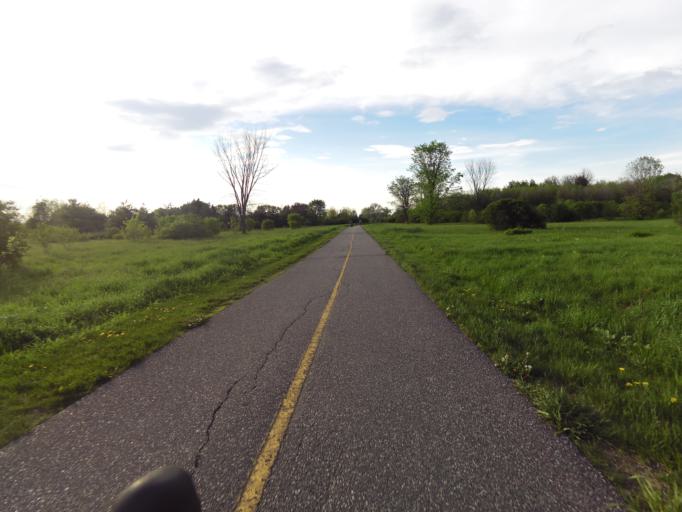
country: CA
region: Ontario
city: Ottawa
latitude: 45.3604
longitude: -75.7606
